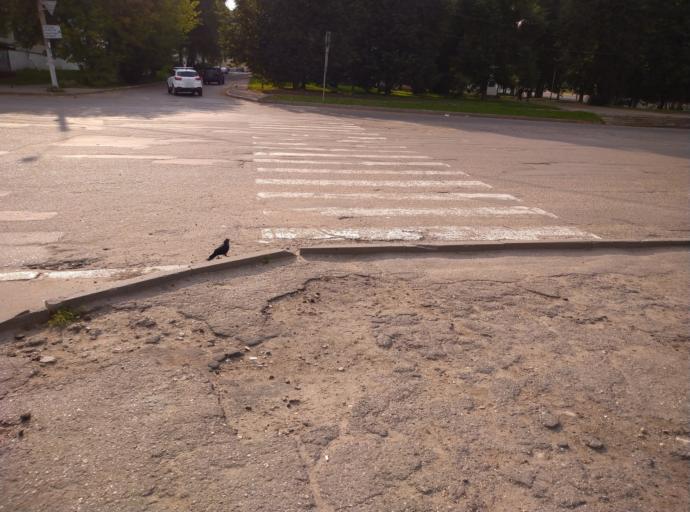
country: RU
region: Kostroma
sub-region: Kostromskoy Rayon
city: Kostroma
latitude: 57.7588
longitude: 40.9612
